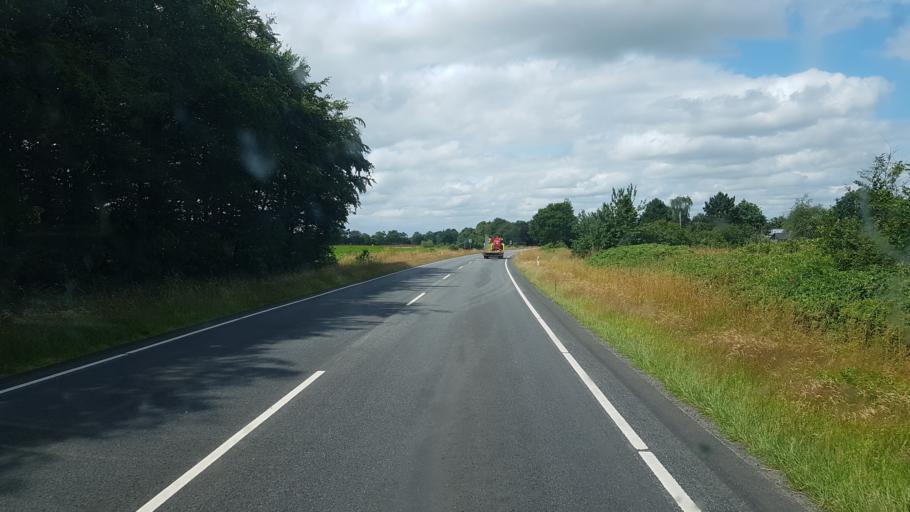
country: DK
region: South Denmark
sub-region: Vejen Kommune
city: Holsted
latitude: 55.5144
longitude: 8.8512
